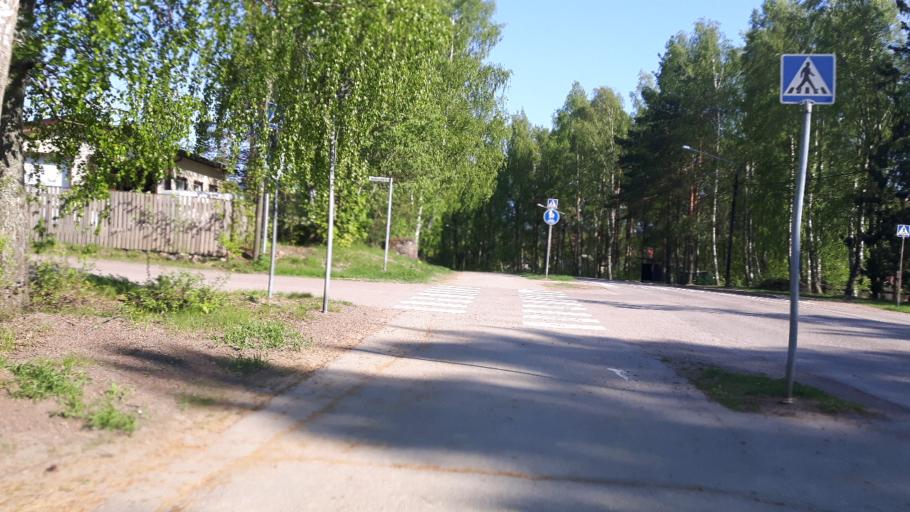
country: FI
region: Kymenlaakso
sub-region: Kotka-Hamina
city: Kotka
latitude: 60.4753
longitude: 26.8723
